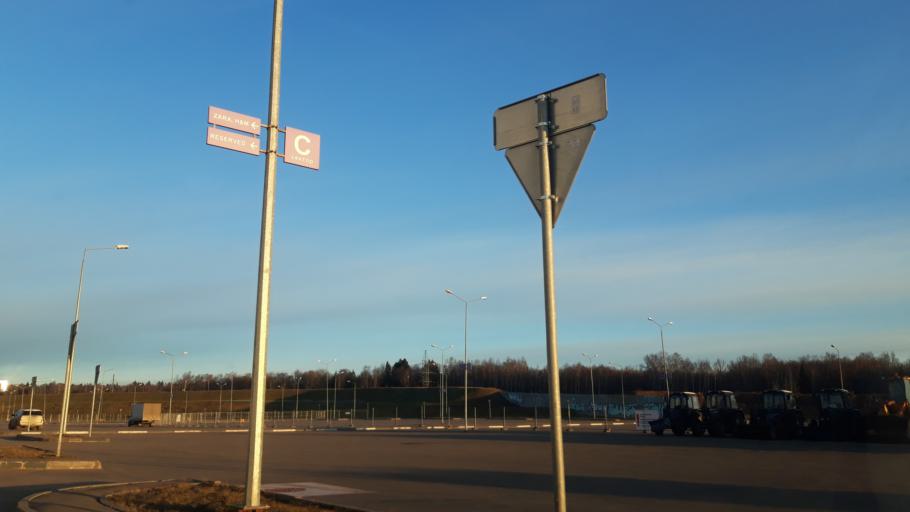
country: RU
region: Moskovskaya
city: Rzhavki
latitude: 55.9973
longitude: 37.2635
